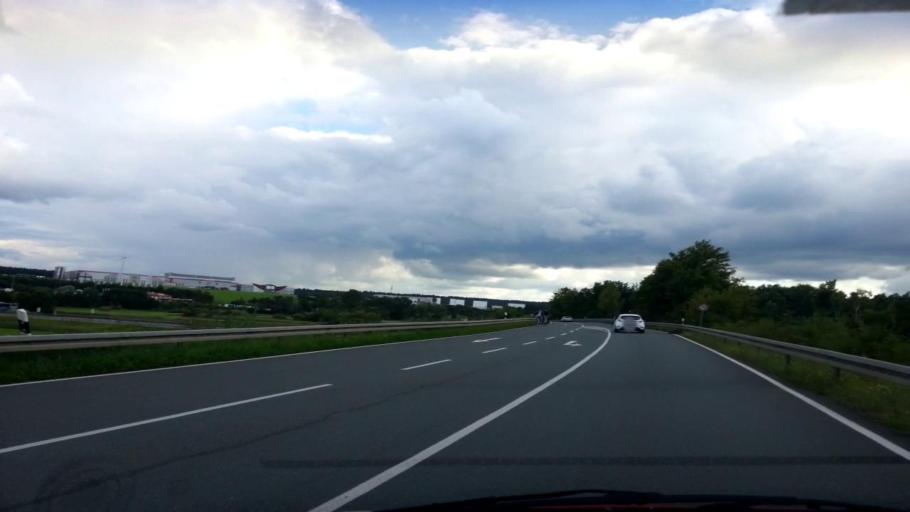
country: DE
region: Bavaria
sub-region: Upper Franconia
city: Schlusselfeld
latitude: 49.7450
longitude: 10.6328
